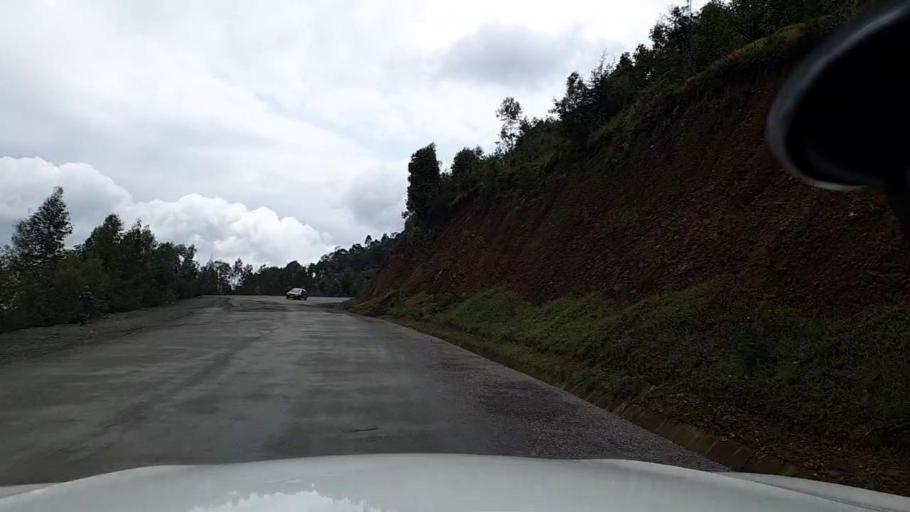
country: RW
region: Western Province
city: Kibuye
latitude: -2.0673
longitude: 29.5459
